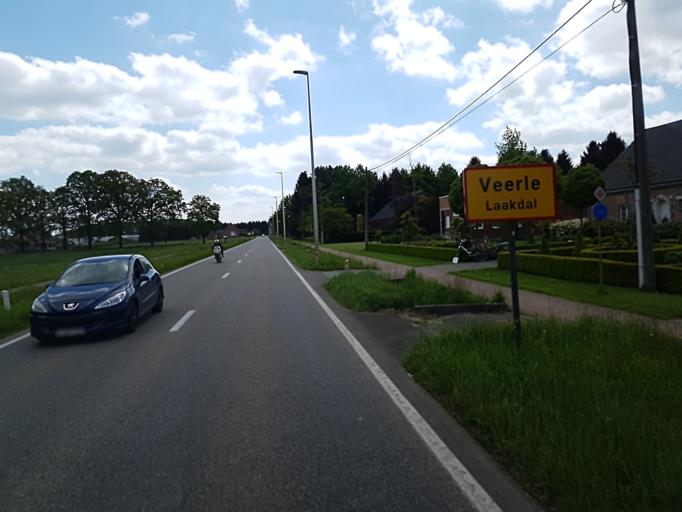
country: BE
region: Flanders
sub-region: Provincie Antwerpen
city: Laakdal
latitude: 51.0751
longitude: 4.9605
